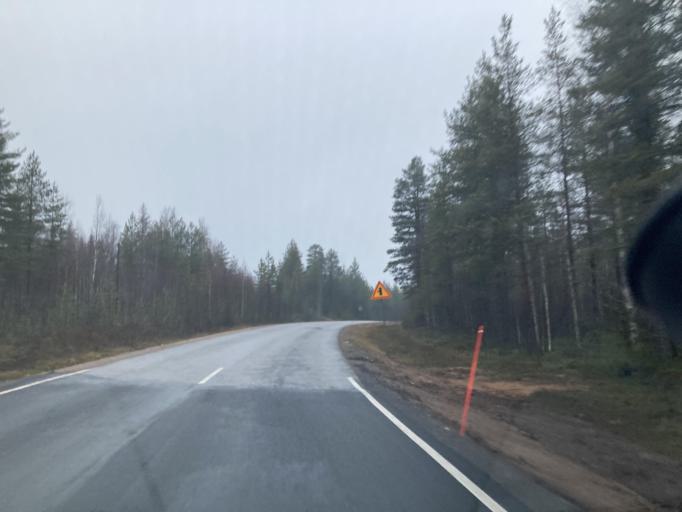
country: FI
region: Lapland
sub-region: Rovaniemi
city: Rovaniemi
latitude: 66.5926
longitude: 25.7926
